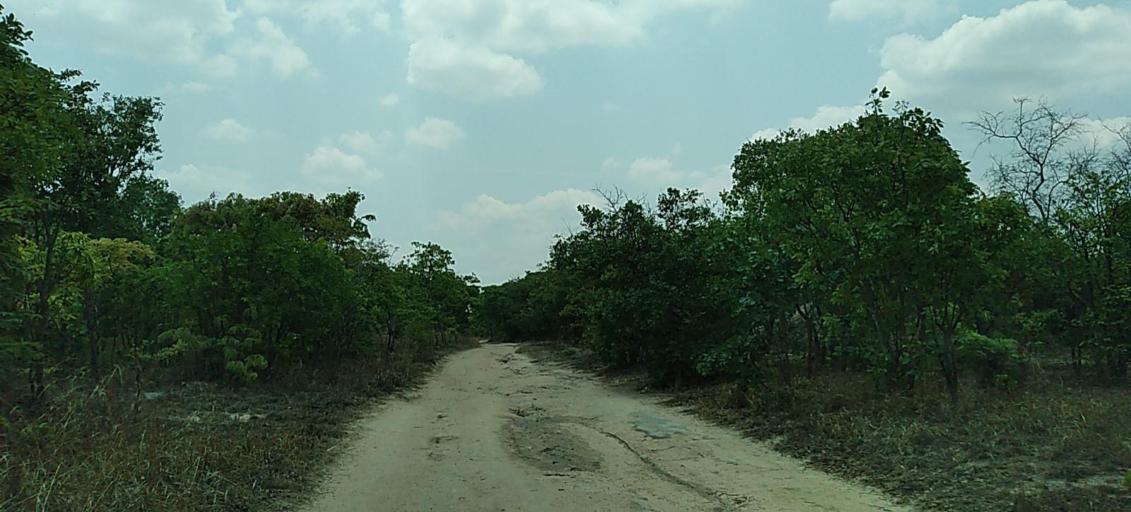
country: ZM
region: Copperbelt
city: Luanshya
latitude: -13.0984
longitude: 28.2953
